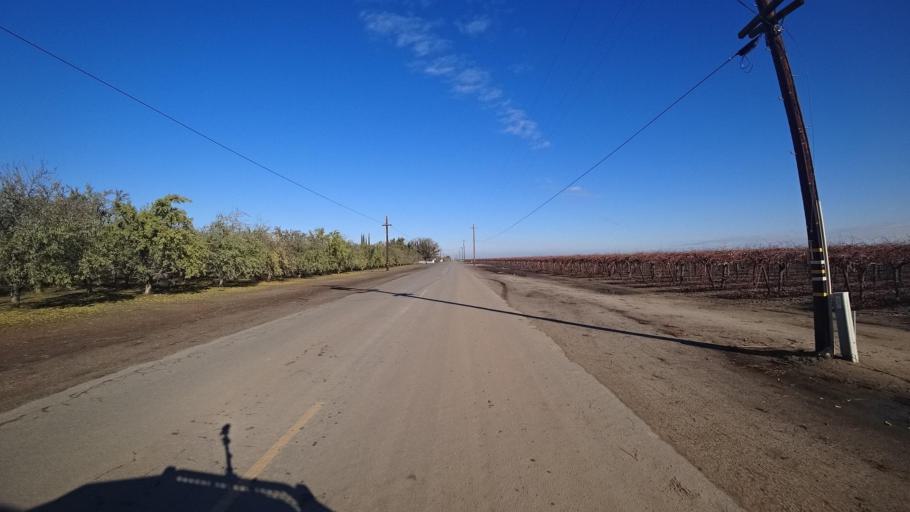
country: US
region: California
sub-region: Kern County
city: McFarland
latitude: 35.7068
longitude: -119.3119
